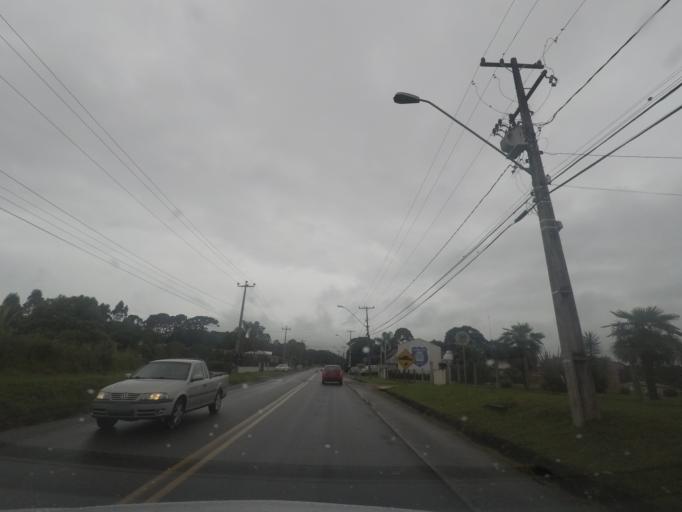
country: BR
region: Parana
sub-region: Campina Grande Do Sul
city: Campina Grande do Sul
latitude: -25.3190
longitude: -49.0758
